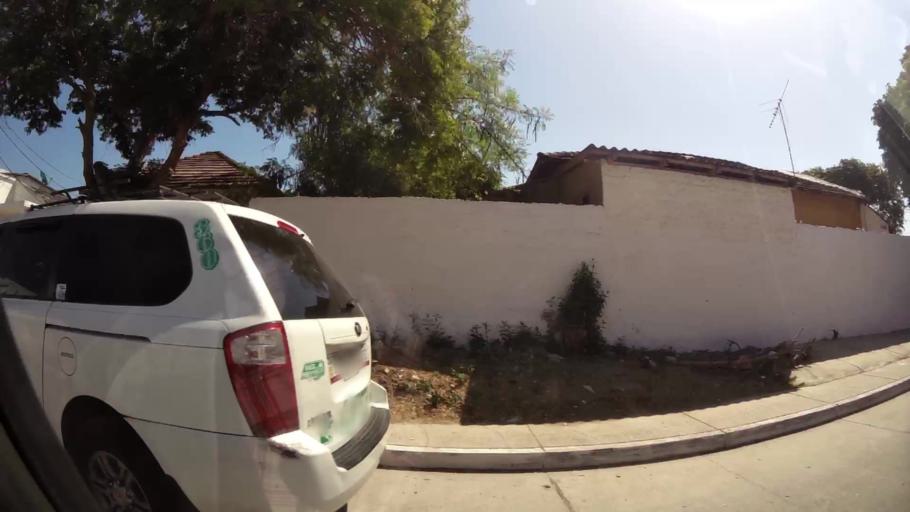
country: CO
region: Bolivar
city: Cartagena
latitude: 10.4391
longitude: -75.5248
